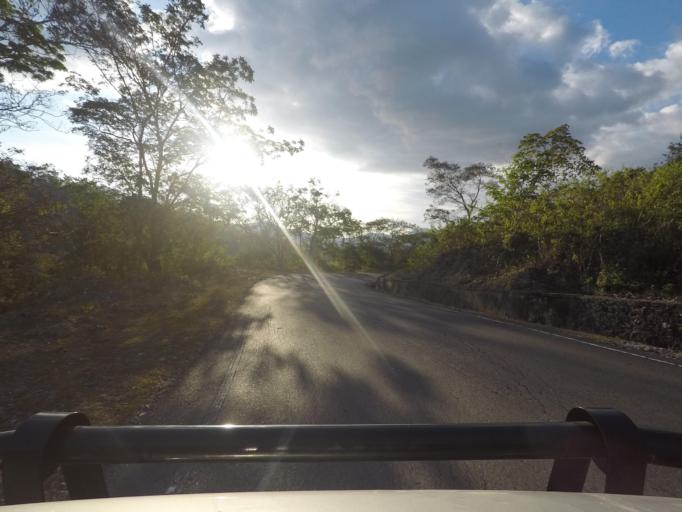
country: TL
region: Bobonaro
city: Maliana
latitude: -8.9521
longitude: 125.0922
